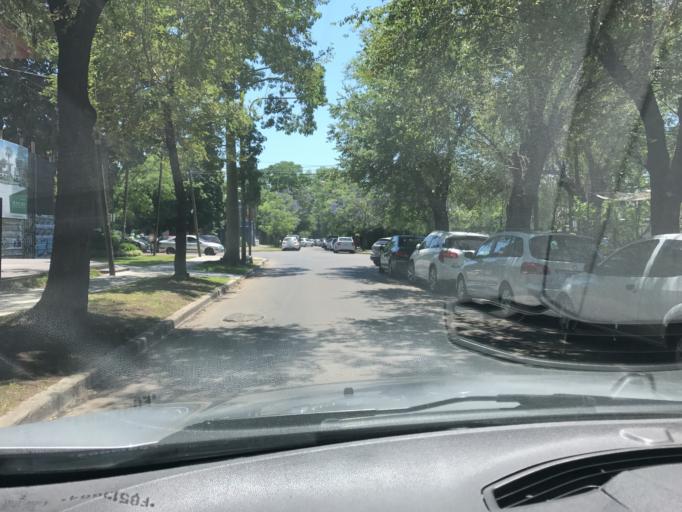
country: AR
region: Buenos Aires
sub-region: Partido de La Plata
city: La Plata
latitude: -34.8679
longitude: -58.0422
